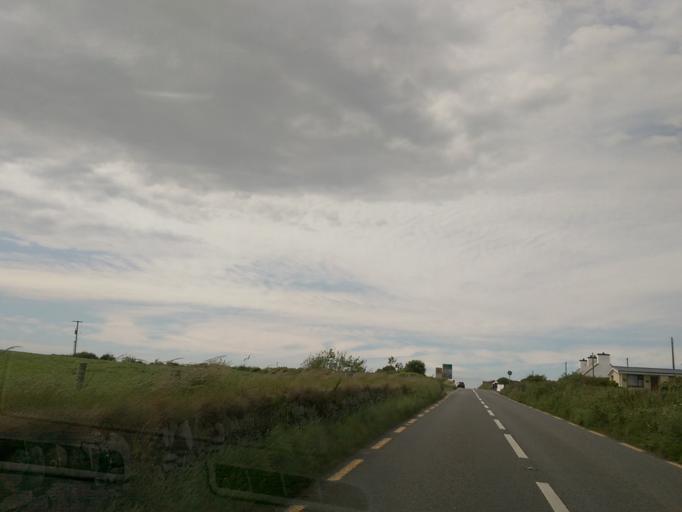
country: IE
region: Munster
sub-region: An Clar
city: Kilrush
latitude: 52.8654
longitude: -9.4146
